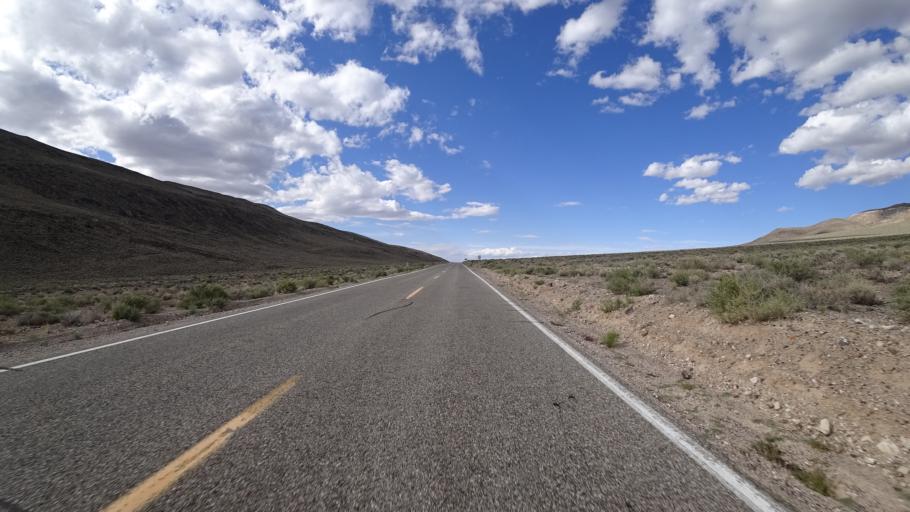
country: US
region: California
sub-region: San Bernardino County
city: Searles Valley
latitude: 36.3950
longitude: -117.2810
